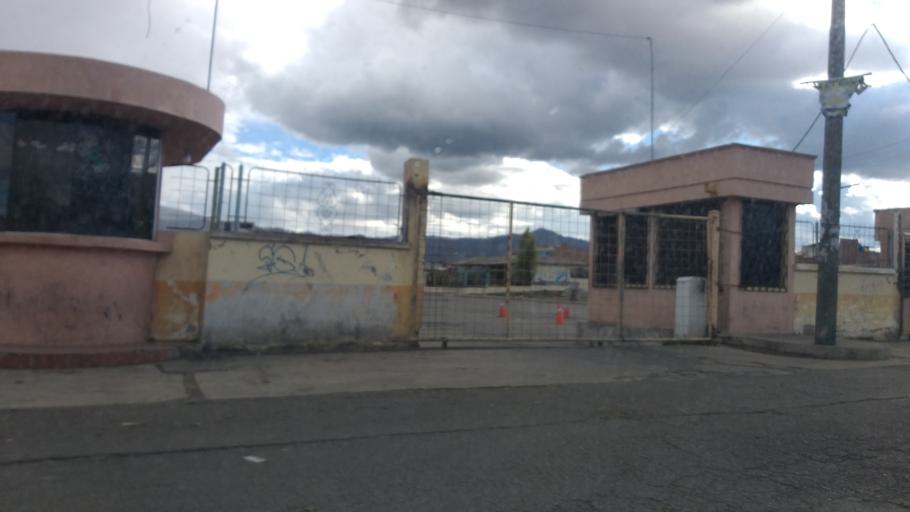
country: EC
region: Chimborazo
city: Riobamba
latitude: -1.6840
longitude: -78.6333
